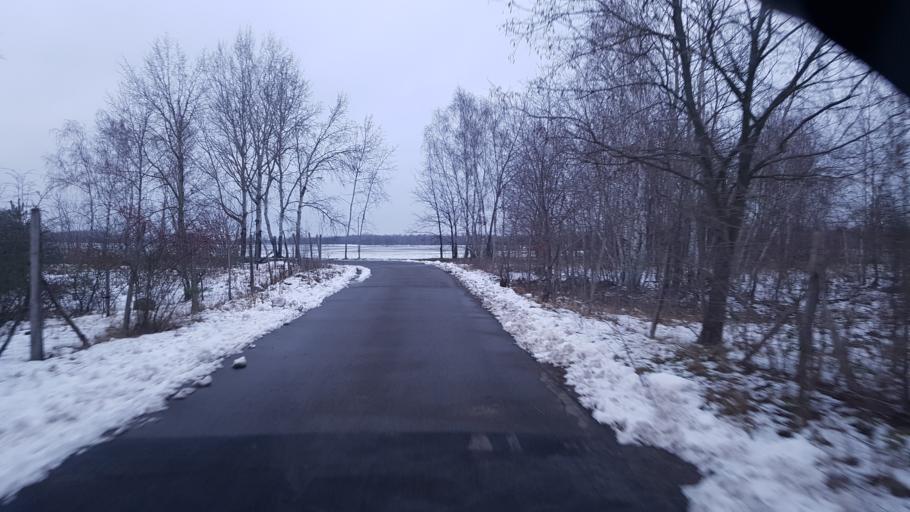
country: DE
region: Brandenburg
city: Vetschau
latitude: 51.7805
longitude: 14.0295
